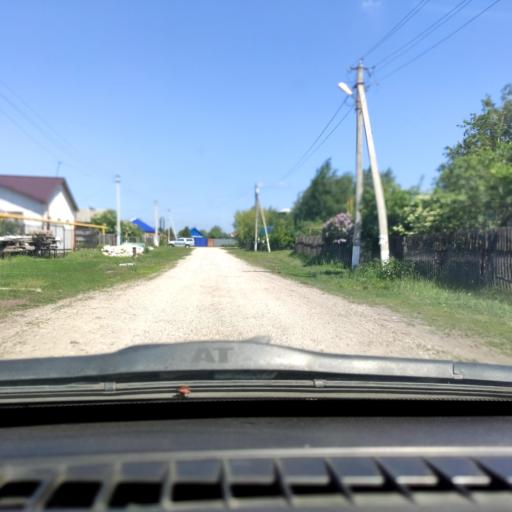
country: RU
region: Samara
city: Povolzhskiy
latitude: 53.5865
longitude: 49.5708
